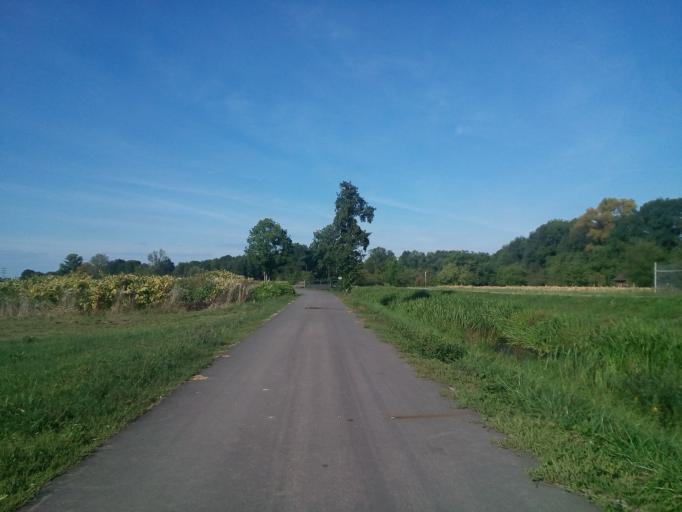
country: DE
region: Baden-Wuerttemberg
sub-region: Karlsruhe Region
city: Zell
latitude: 48.6646
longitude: 8.0742
